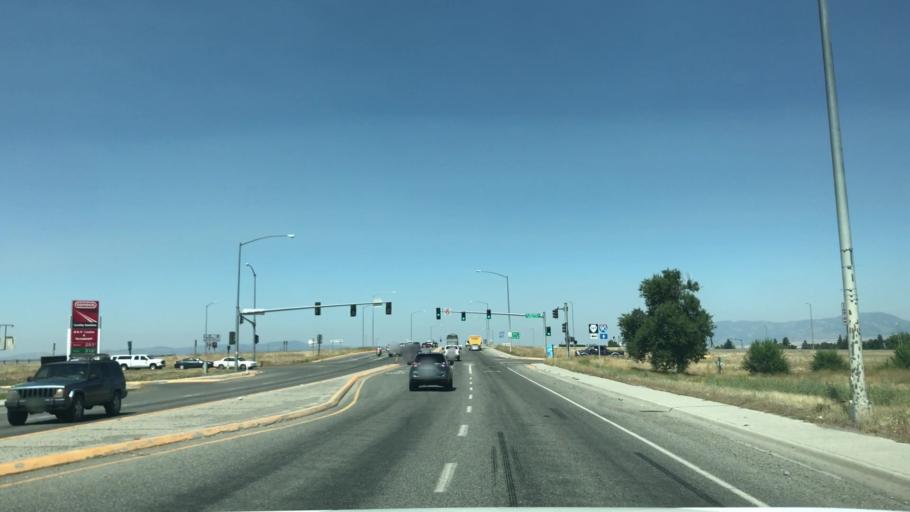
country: US
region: Montana
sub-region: Gallatin County
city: Belgrade
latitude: 45.7649
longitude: -111.1851
